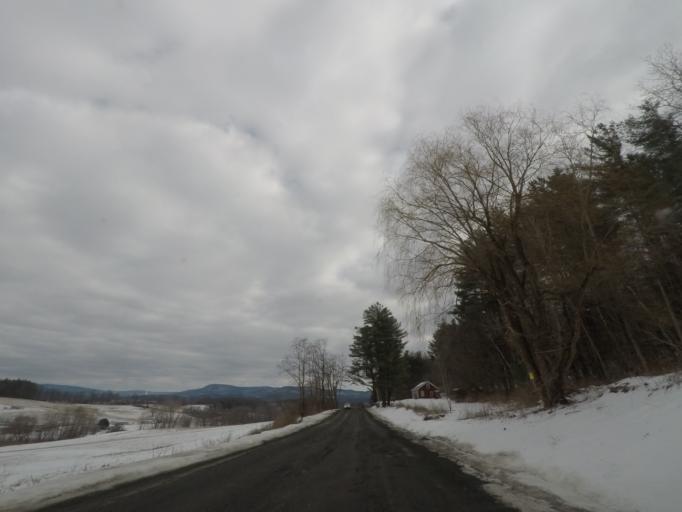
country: US
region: New York
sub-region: Rensselaer County
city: Hoosick Falls
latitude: 42.8651
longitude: -73.3673
